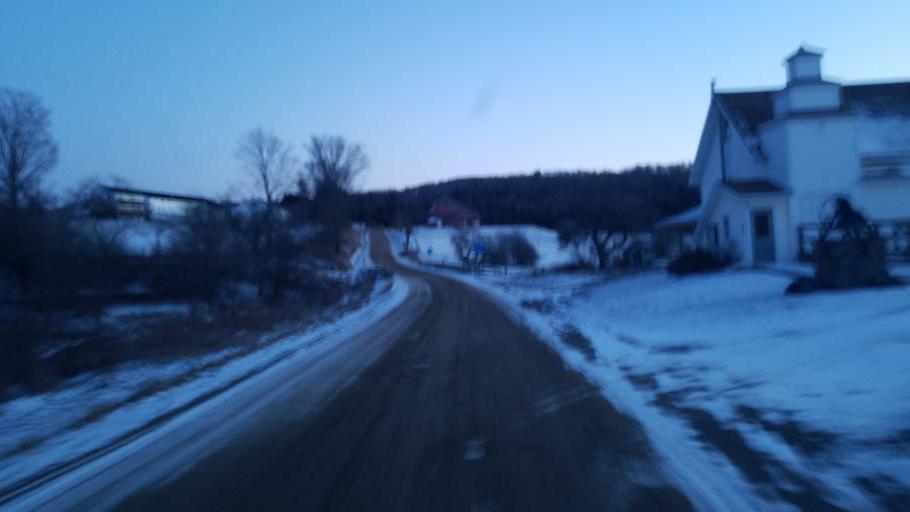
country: US
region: New York
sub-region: Allegany County
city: Andover
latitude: 41.9533
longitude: -77.7769
